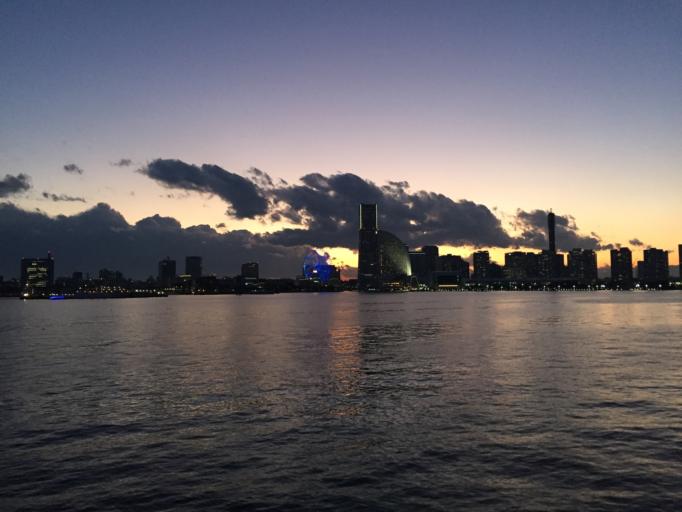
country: JP
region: Kanagawa
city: Yokohama
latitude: 35.4628
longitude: 139.6514
